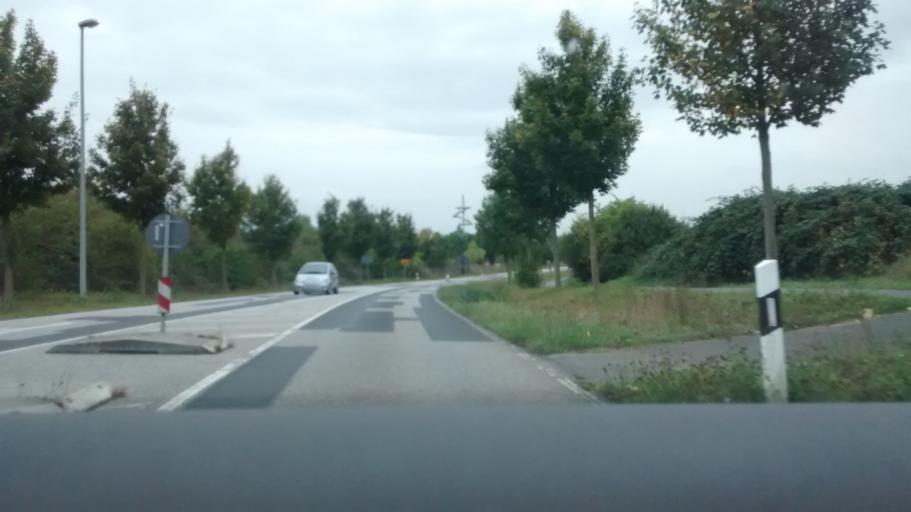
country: DE
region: Mecklenburg-Vorpommern
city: Wismar
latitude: 53.8905
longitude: 11.4251
